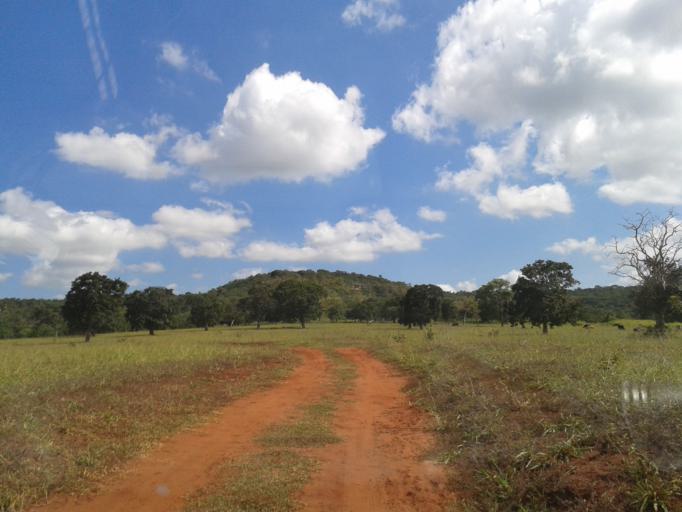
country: BR
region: Minas Gerais
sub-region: Santa Vitoria
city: Santa Vitoria
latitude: -19.2525
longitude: -50.0601
